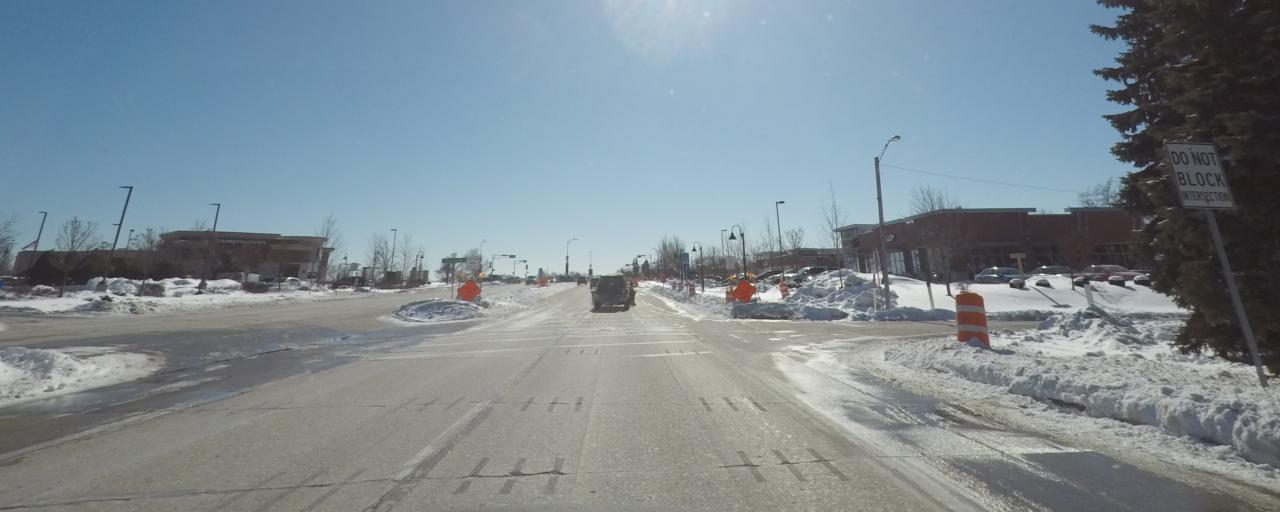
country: US
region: Wisconsin
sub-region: Waukesha County
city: New Berlin
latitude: 42.9779
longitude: -88.1086
